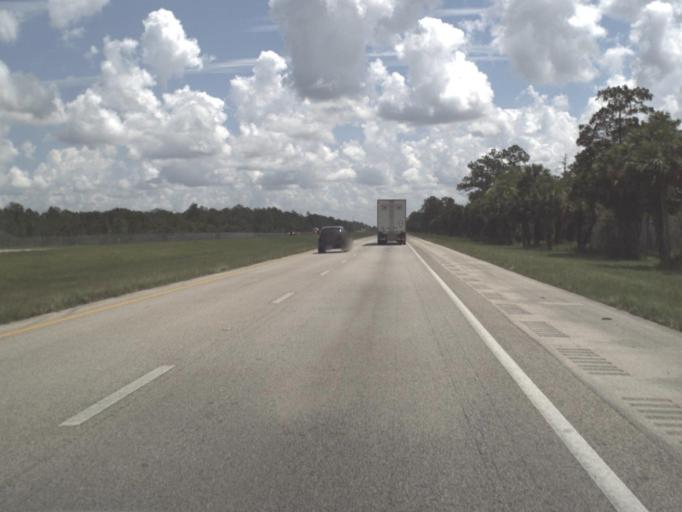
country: US
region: Florida
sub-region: Collier County
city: Orangetree
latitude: 26.1530
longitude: -81.4796
